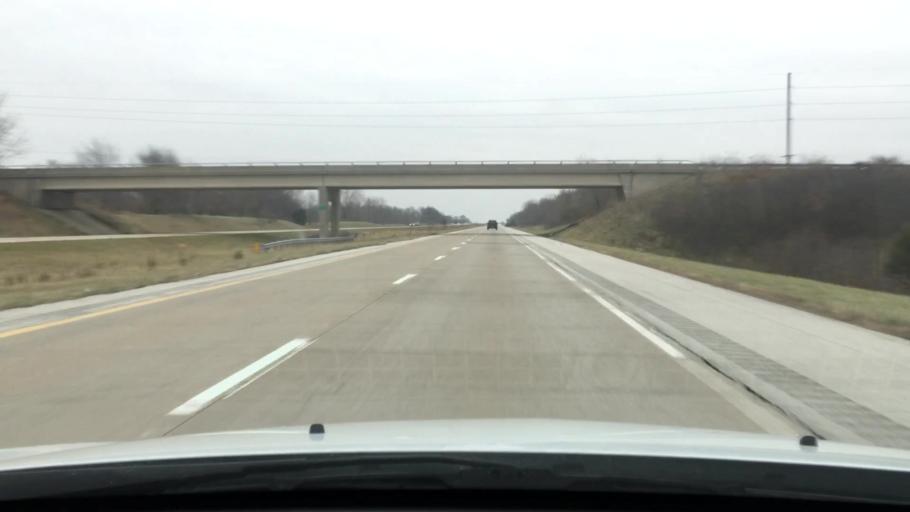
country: US
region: Illinois
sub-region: Scott County
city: Winchester
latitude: 39.6810
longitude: -90.5044
